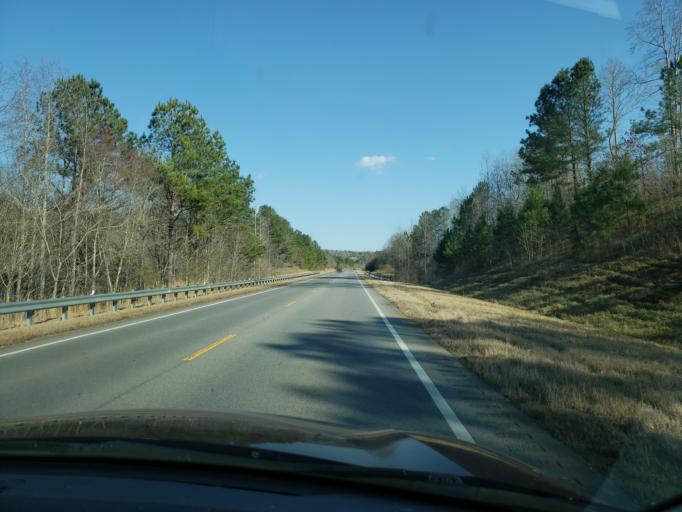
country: US
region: Alabama
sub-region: Cleburne County
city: Heflin
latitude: 33.5048
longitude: -85.6152
